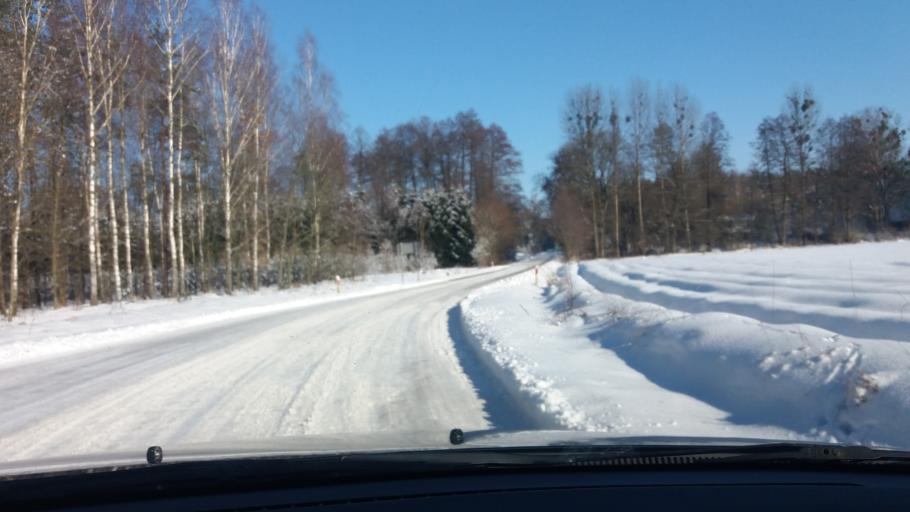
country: PL
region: Warmian-Masurian Voivodeship
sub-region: Powiat nidzicki
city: Nidzica
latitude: 53.3510
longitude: 20.6140
